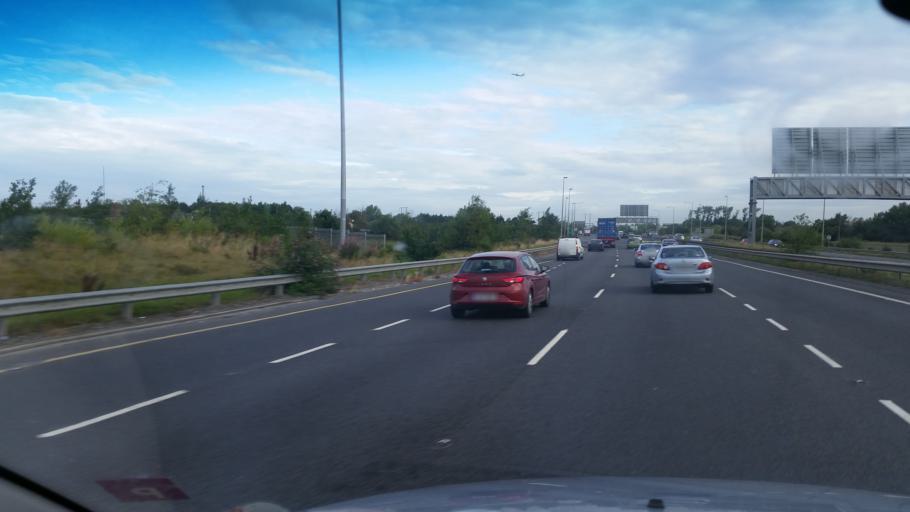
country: IE
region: Leinster
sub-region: Dublin City
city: Finglas
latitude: 53.4061
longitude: -6.3125
